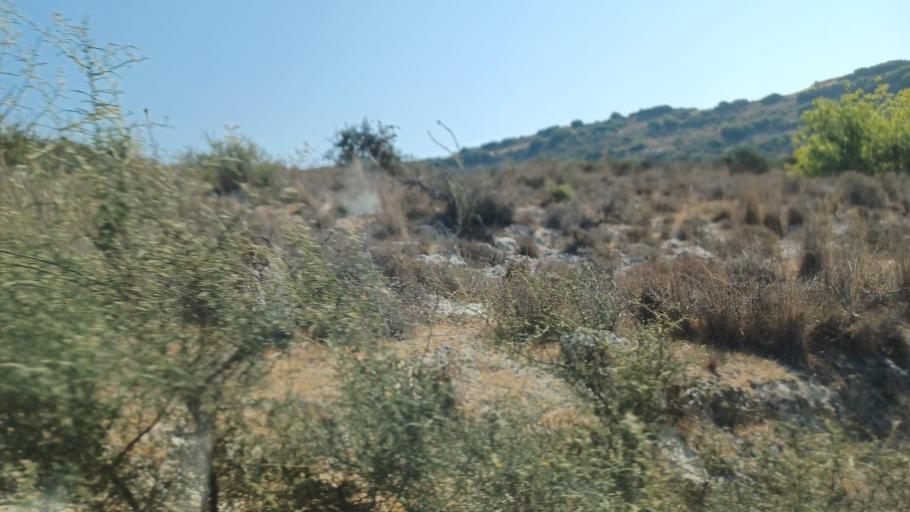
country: CY
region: Pafos
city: Mesogi
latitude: 34.8754
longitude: 32.5308
